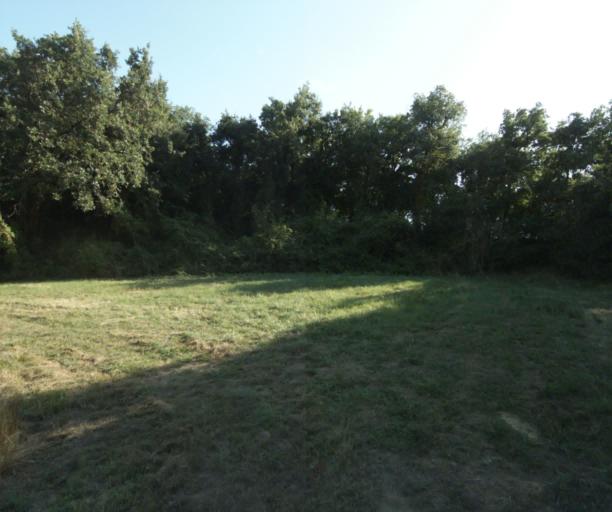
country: FR
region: Midi-Pyrenees
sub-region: Departement de la Haute-Garonne
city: Saint-Felix-Lauragais
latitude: 43.4322
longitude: 1.8253
